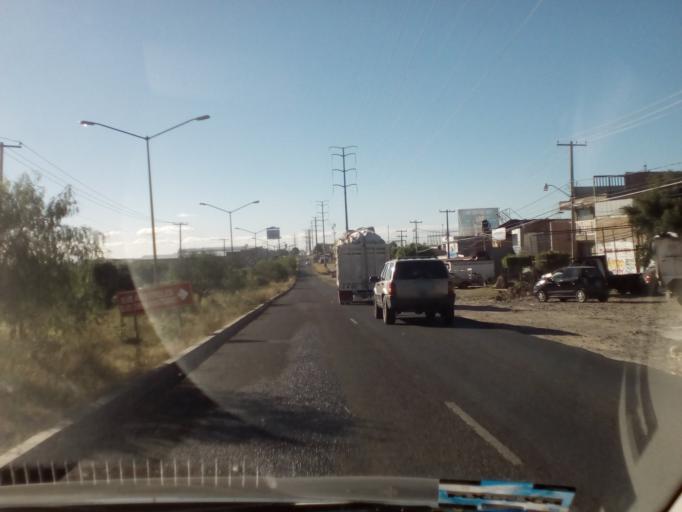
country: MX
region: Guanajuato
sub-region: Leon
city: La Ermita
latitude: 21.1509
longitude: -101.7292
